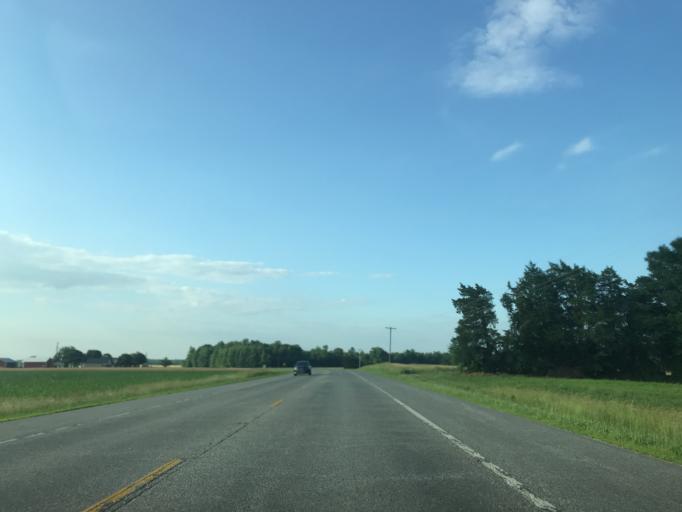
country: US
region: Maryland
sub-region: Caroline County
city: Denton
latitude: 38.8208
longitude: -75.7788
